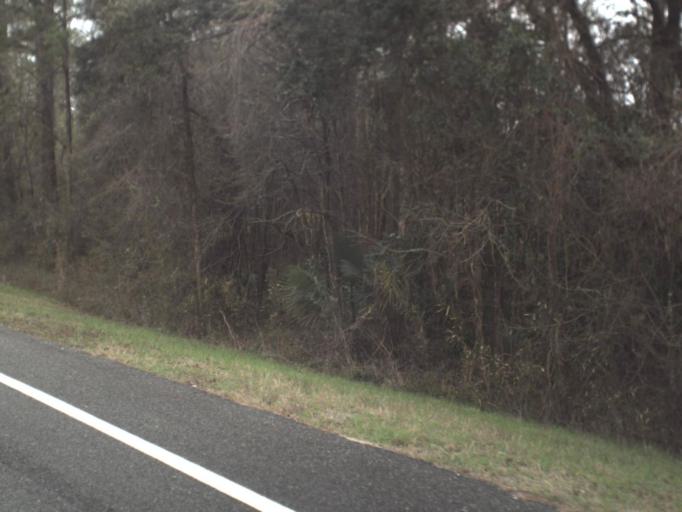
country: US
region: Florida
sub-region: Leon County
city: Woodville
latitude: 30.4071
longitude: -84.0627
